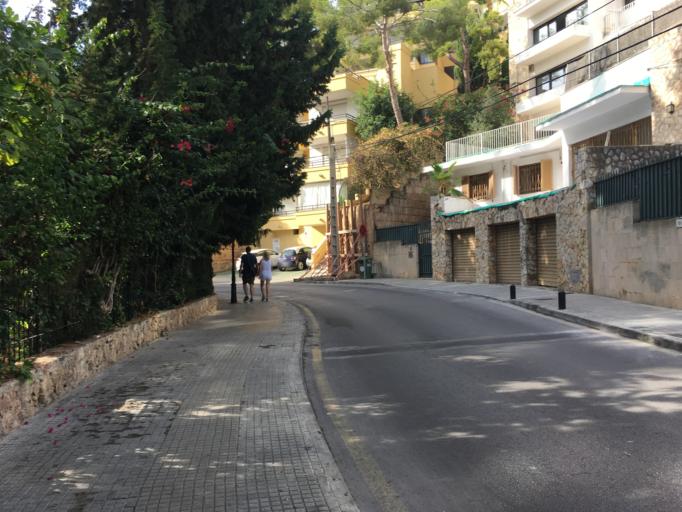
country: ES
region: Balearic Islands
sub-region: Illes Balears
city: Magaluf
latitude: 39.5396
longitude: 2.5914
